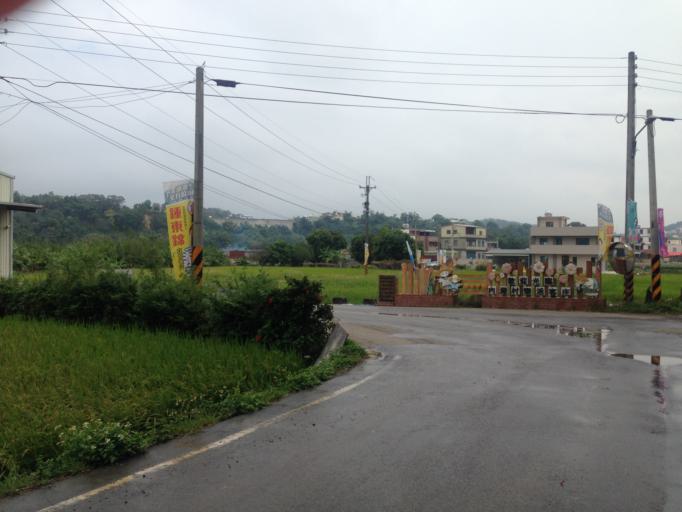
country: TW
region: Taiwan
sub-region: Hsinchu
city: Hsinchu
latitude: 24.6750
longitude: 120.9520
